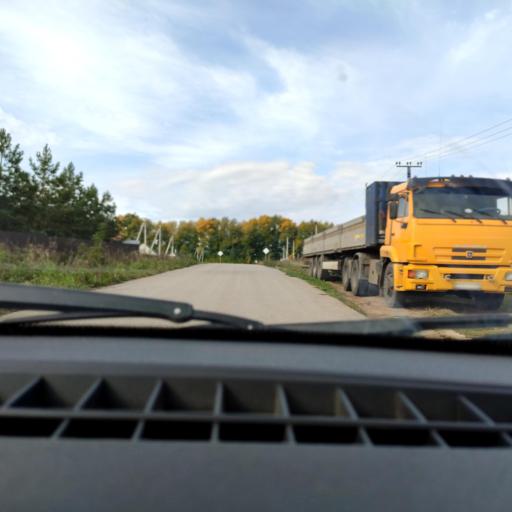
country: RU
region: Bashkortostan
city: Avdon
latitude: 54.6560
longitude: 55.7341
